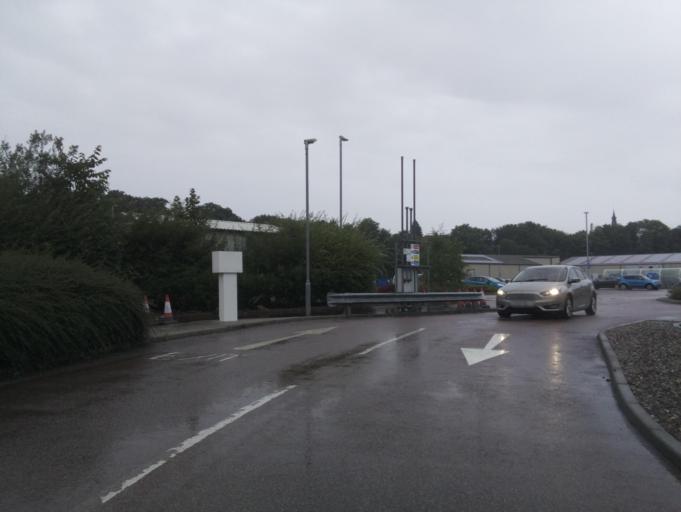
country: GB
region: Scotland
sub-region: Perth and Kinross
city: Blairgowrie
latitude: 56.5887
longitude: -3.3337
